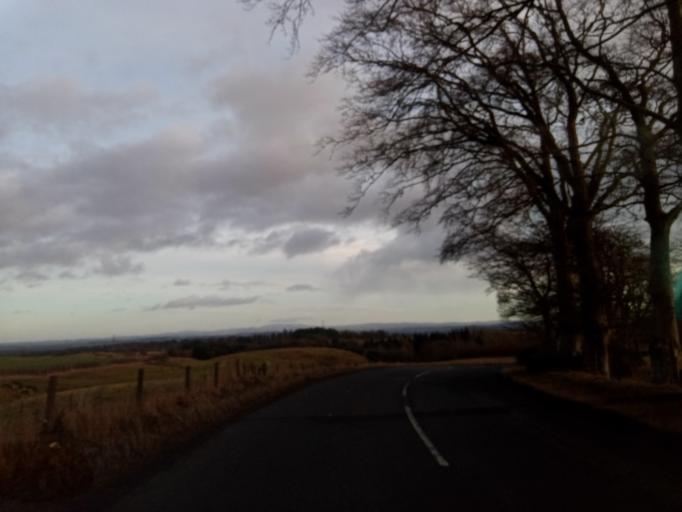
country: GB
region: Scotland
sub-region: The Scottish Borders
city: Melrose
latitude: 55.5520
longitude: -2.7621
